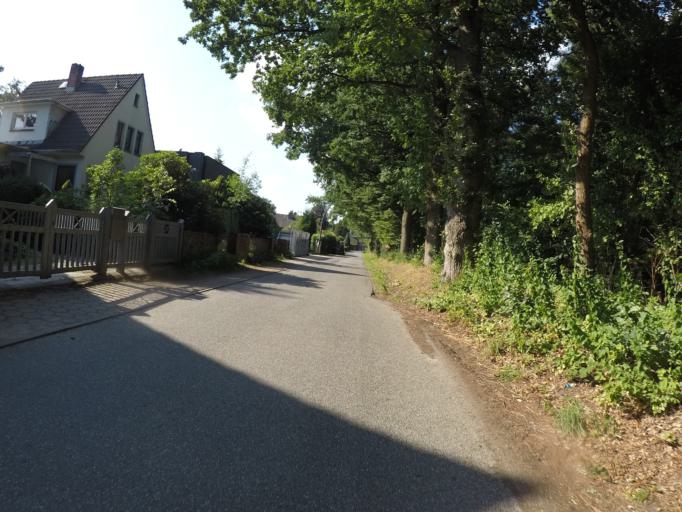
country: DE
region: Hamburg
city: Sasel
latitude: 53.6348
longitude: 10.1293
